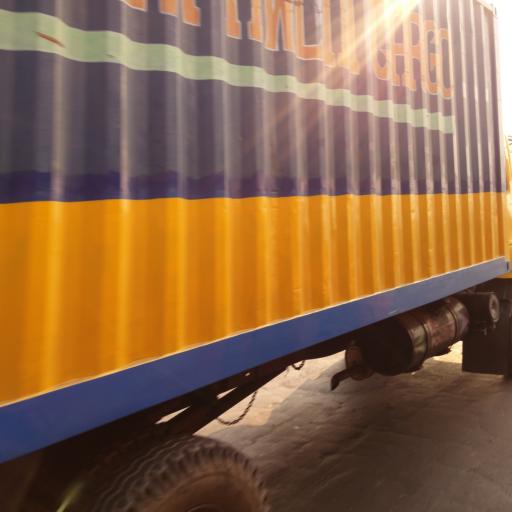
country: BD
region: Dhaka
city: Tungi
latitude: 23.8942
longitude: 90.3504
